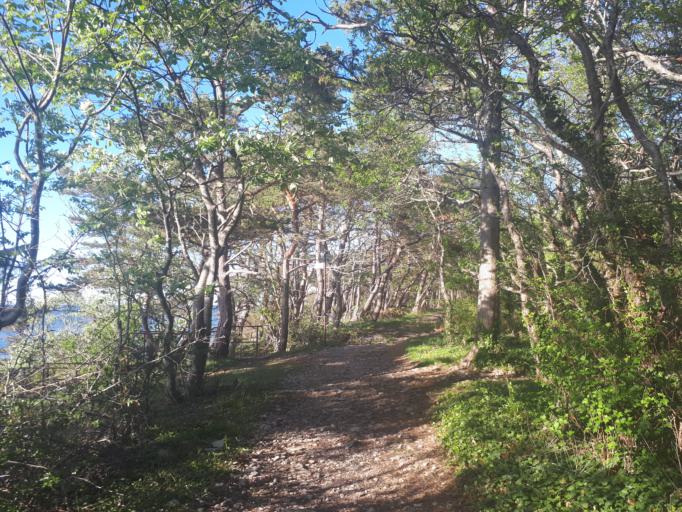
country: SE
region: Gotland
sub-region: Gotland
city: Vibble
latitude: 57.6126
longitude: 18.2475
